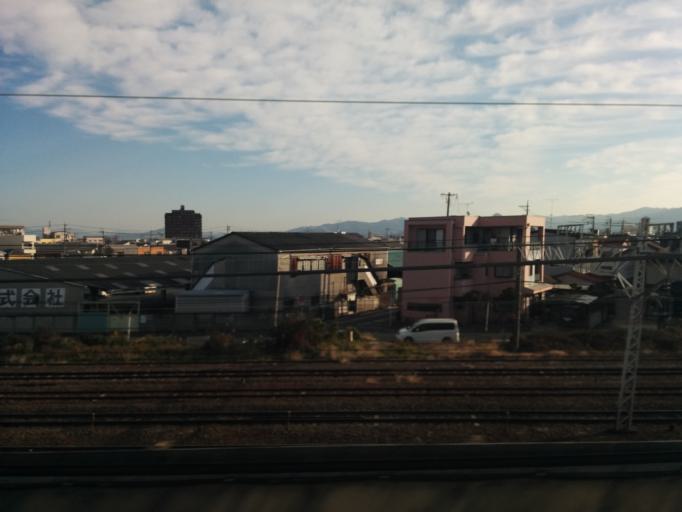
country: JP
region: Aichi
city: Toyohashi
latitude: 34.7708
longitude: 137.3768
